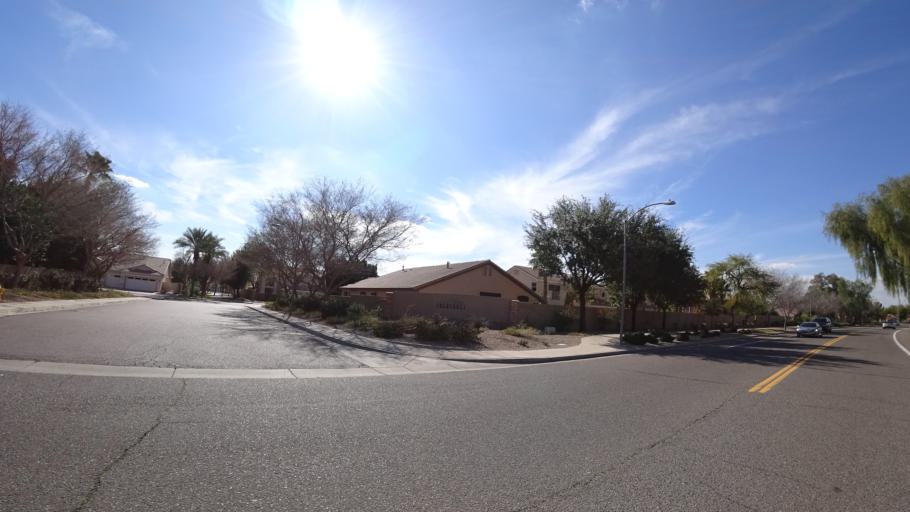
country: US
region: Arizona
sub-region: Maricopa County
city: Peoria
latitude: 33.6722
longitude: -112.2095
